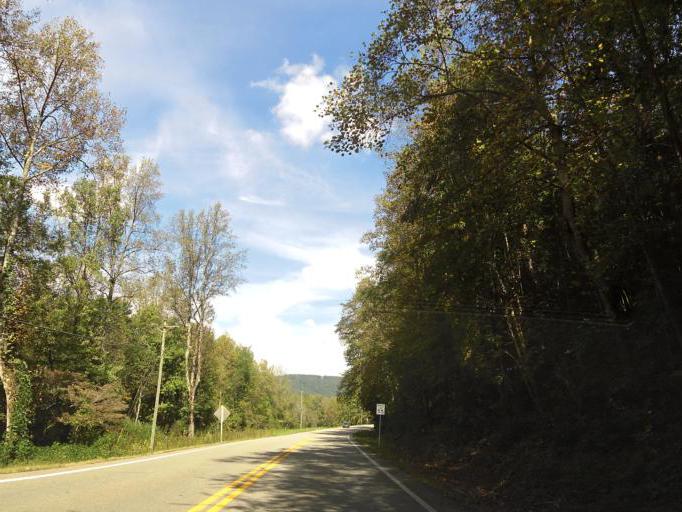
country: US
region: Georgia
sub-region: Pickens County
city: Jasper
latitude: 34.5406
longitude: -84.2634
